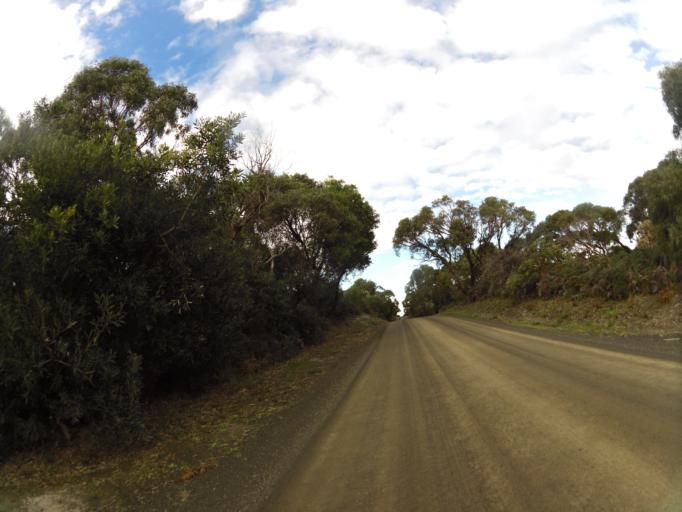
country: AU
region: Victoria
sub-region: Bass Coast
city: North Wonthaggi
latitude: -38.6253
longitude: 145.5653
